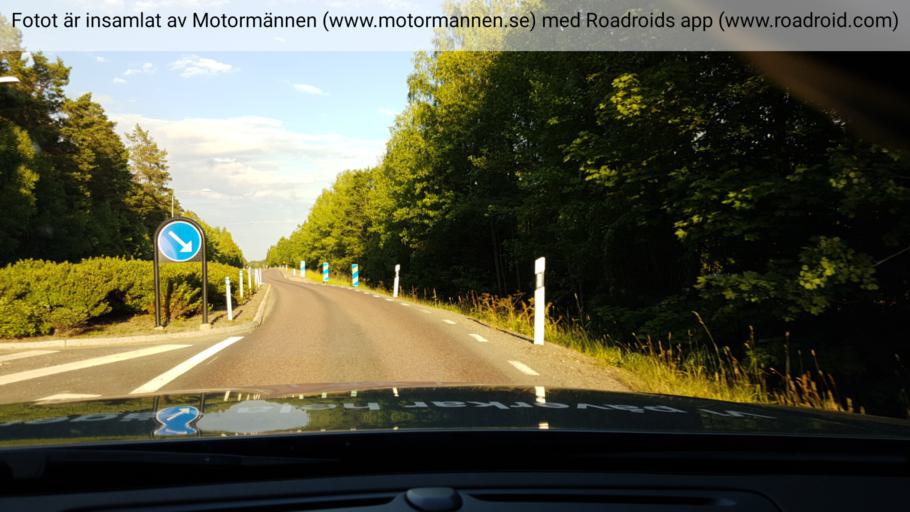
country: SE
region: Uppsala
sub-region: Enkopings Kommun
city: Orsundsbro
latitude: 59.8845
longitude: 17.2099
